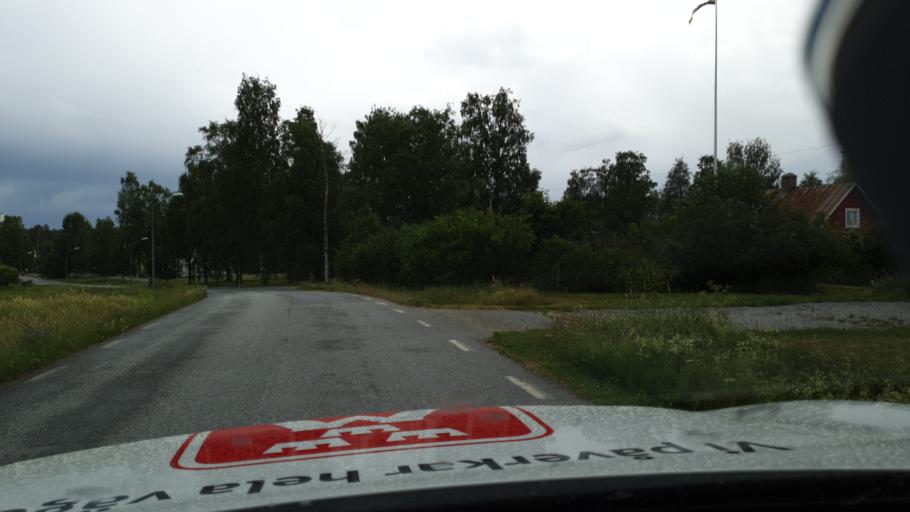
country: SE
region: Vaesterbotten
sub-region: Dorotea Kommun
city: Dorotea
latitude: 63.8162
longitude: 16.4000
